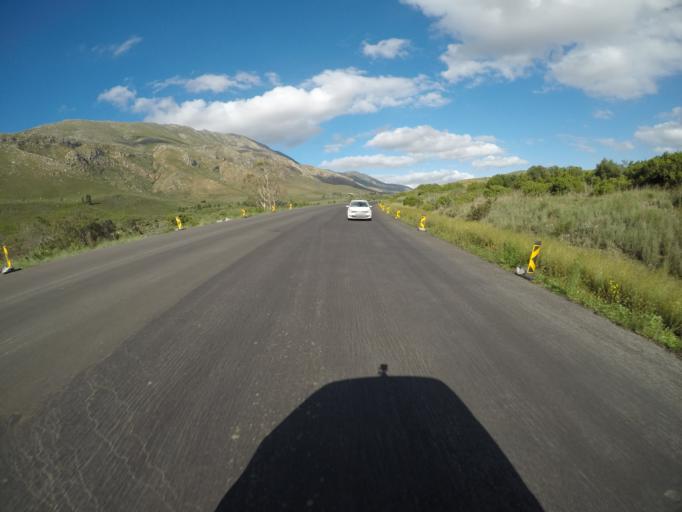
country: ZA
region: Western Cape
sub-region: Cape Winelands District Municipality
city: Ashton
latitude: -33.8735
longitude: 20.1606
